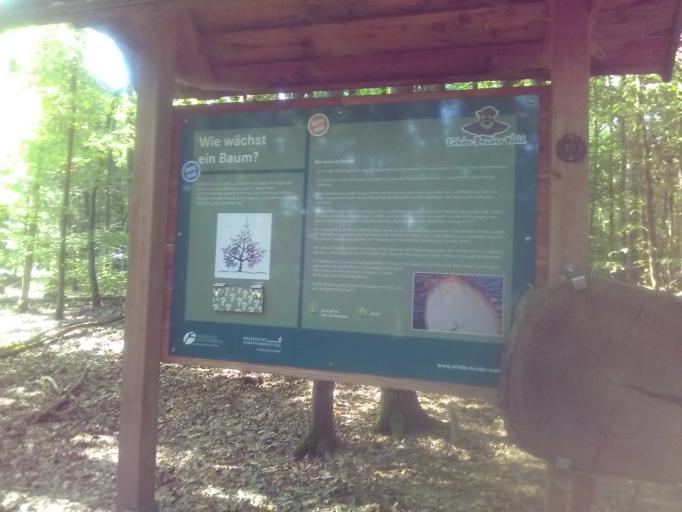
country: DE
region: Bavaria
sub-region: Upper Franconia
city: Bamberg
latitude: 49.8666
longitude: 10.8981
